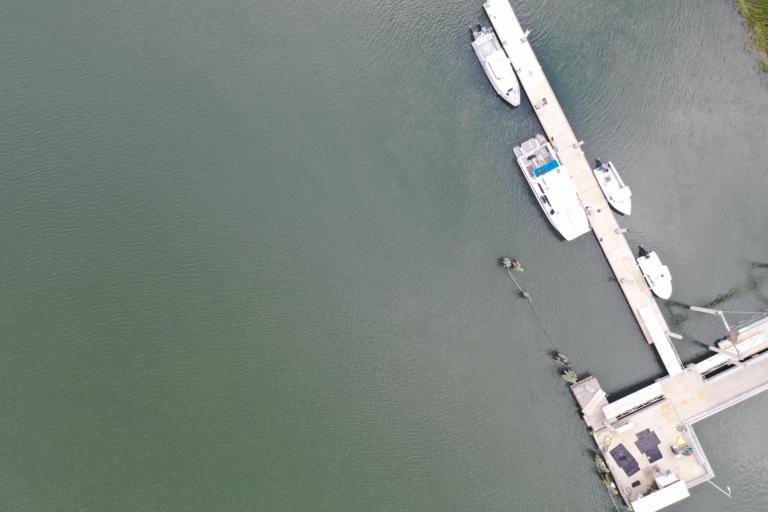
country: US
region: Georgia
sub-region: Chatham County
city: Whitemarsh Island
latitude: 31.9901
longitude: -81.0226
